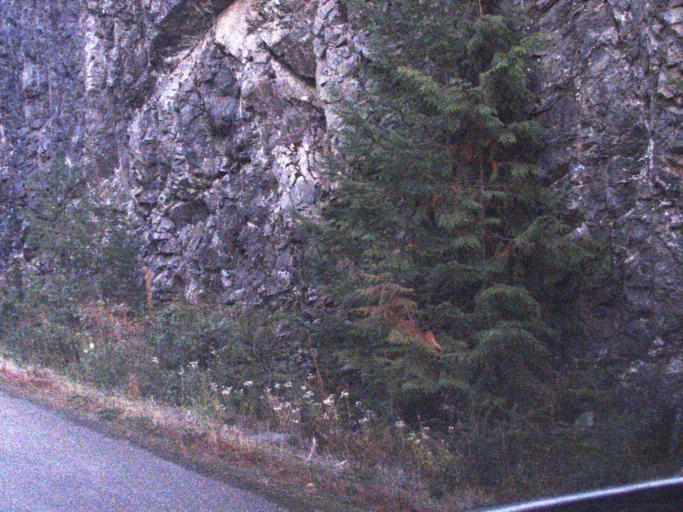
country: US
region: Washington
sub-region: Snohomish County
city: Darrington
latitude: 48.7062
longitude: -120.9590
